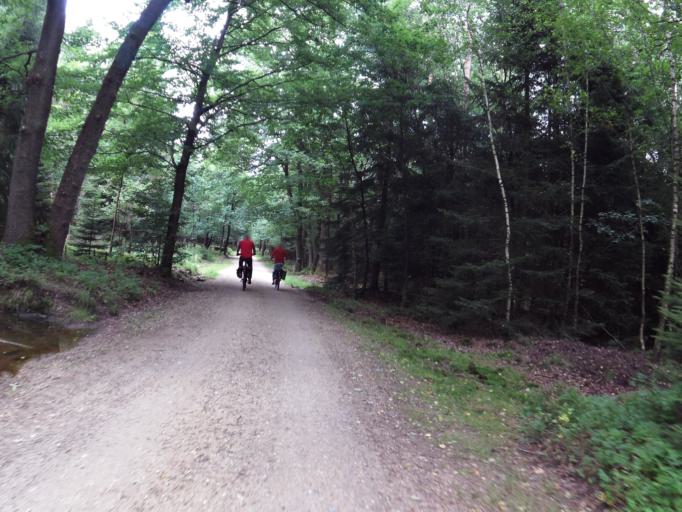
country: NL
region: Gelderland
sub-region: Gemeente Apeldoorn
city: Loenen
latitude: 52.0975
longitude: 6.0055
